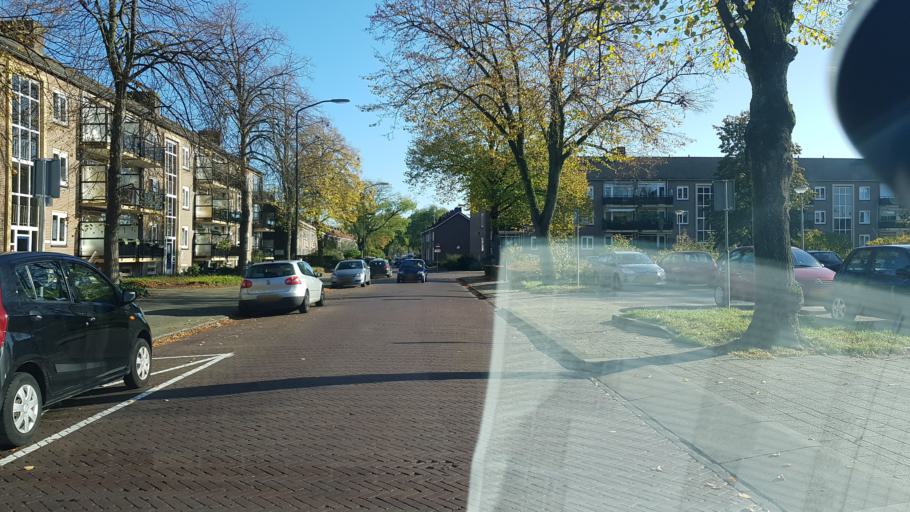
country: NL
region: Gelderland
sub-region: Gemeente Apeldoorn
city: Apeldoorn
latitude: 52.1906
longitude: 5.9664
